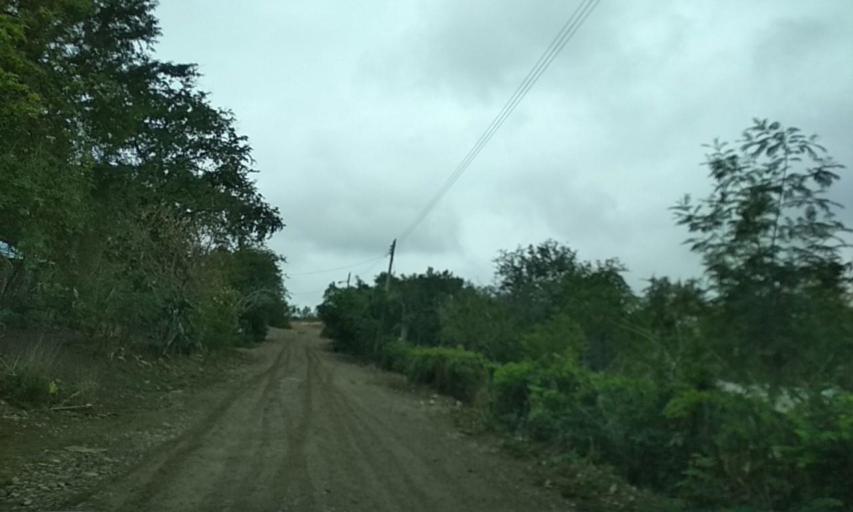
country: MX
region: Veracruz
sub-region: Papantla
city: El Chote
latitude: 20.3828
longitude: -97.3559
